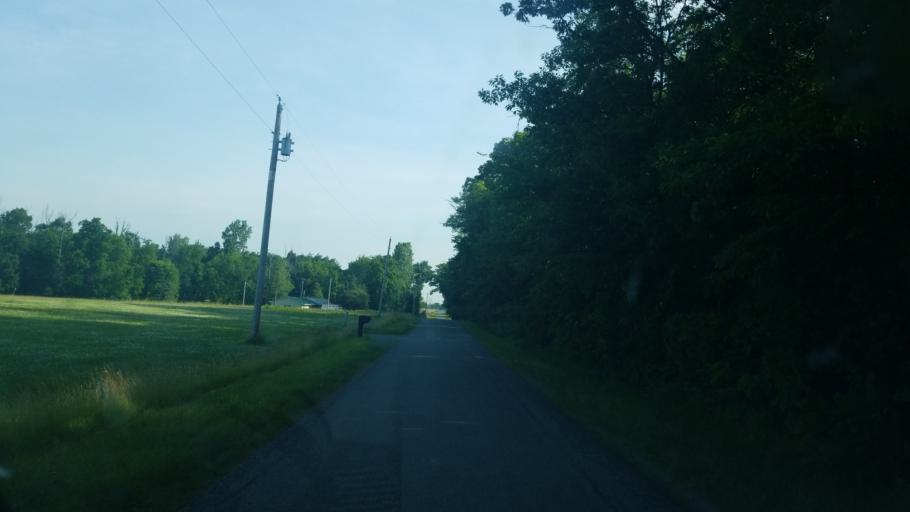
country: US
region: Ohio
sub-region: Hancock County
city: Arlington
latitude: 40.8388
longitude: -83.6704
